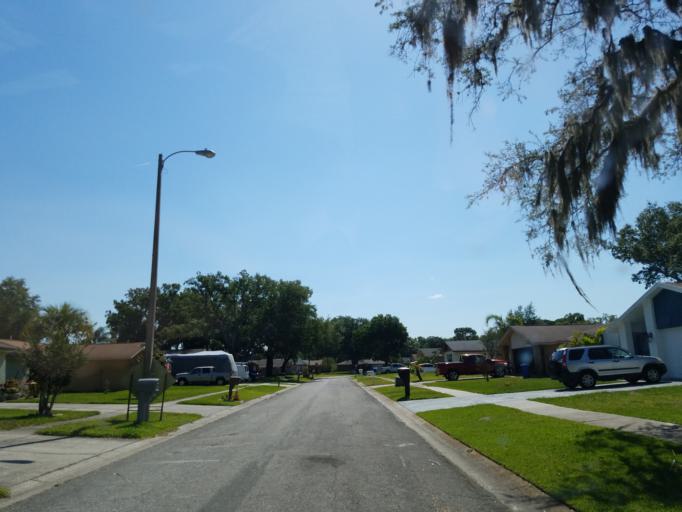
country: US
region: Florida
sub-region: Hillsborough County
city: Riverview
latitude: 27.8874
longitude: -82.2963
